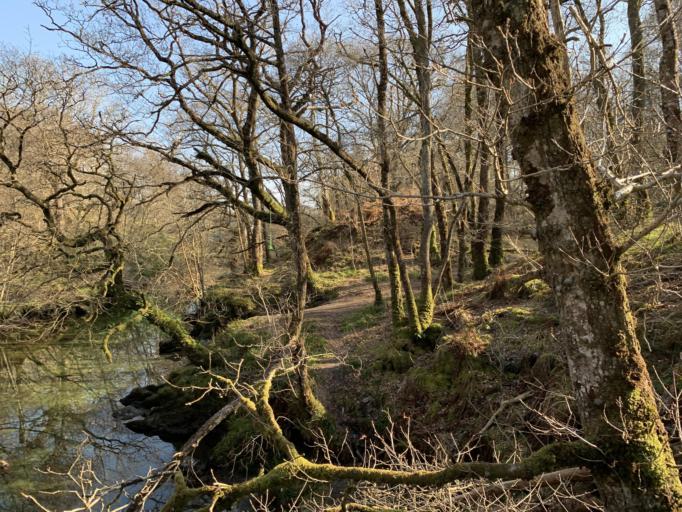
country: GB
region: Scotland
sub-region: West Dunbartonshire
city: Balloch
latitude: 56.1008
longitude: -4.6451
